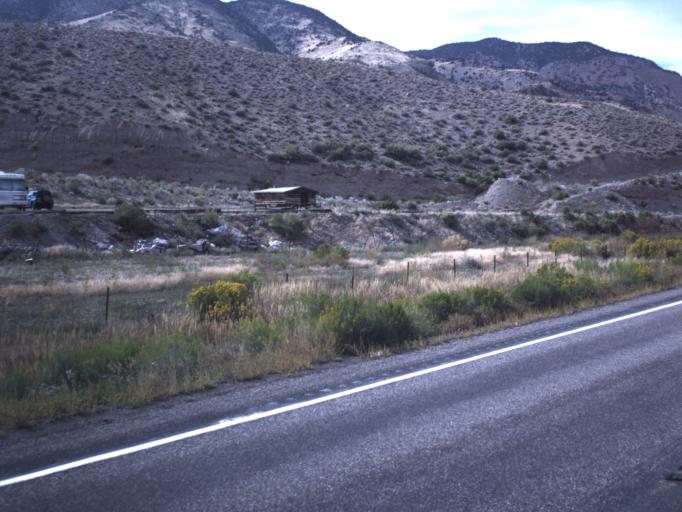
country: US
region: Utah
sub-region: Sevier County
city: Monroe
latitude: 38.4742
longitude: -112.2380
